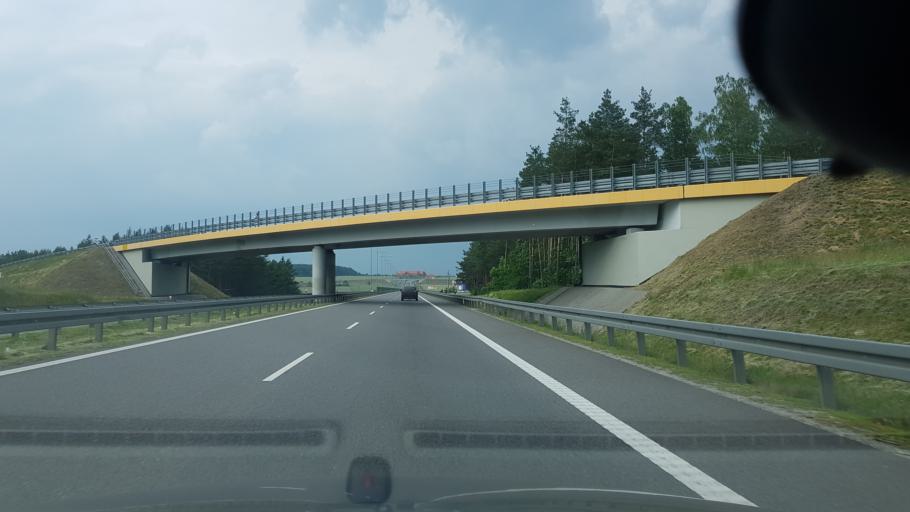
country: PL
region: Masovian Voivodeship
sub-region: Powiat legionowski
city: Serock
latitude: 52.5237
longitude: 21.0568
